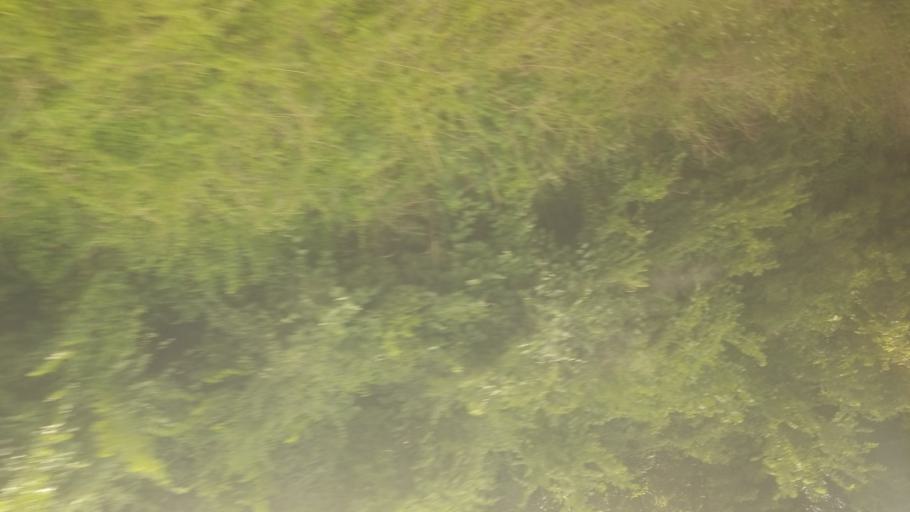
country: US
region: Missouri
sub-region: Jackson County
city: Sugar Creek
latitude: 39.1308
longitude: -94.4329
